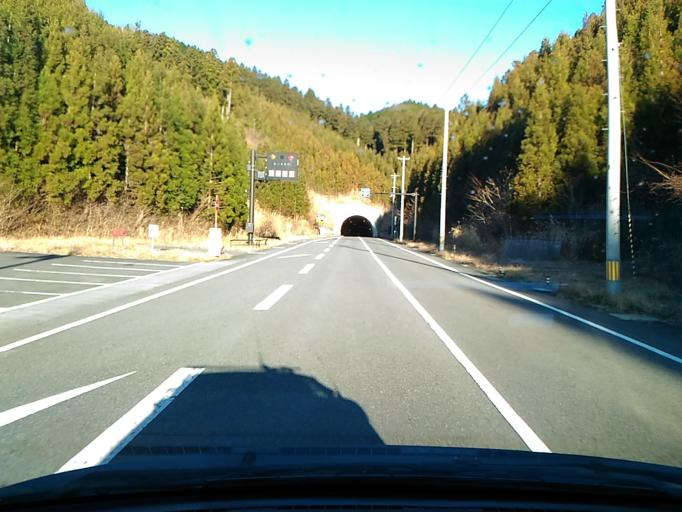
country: JP
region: Ibaraki
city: Kitaibaraki
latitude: 36.9656
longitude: 140.6171
